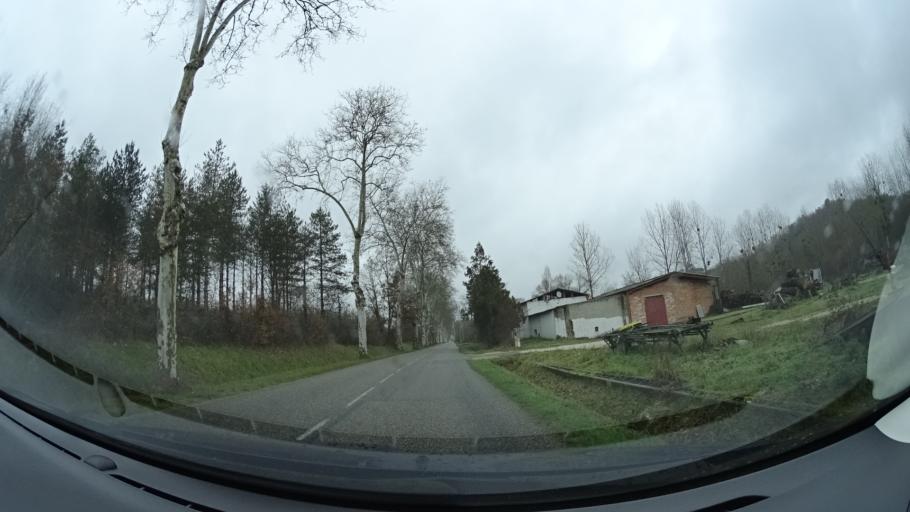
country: FR
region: Midi-Pyrenees
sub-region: Departement du Tarn-et-Garonne
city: Moissac
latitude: 44.1483
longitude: 1.1008
